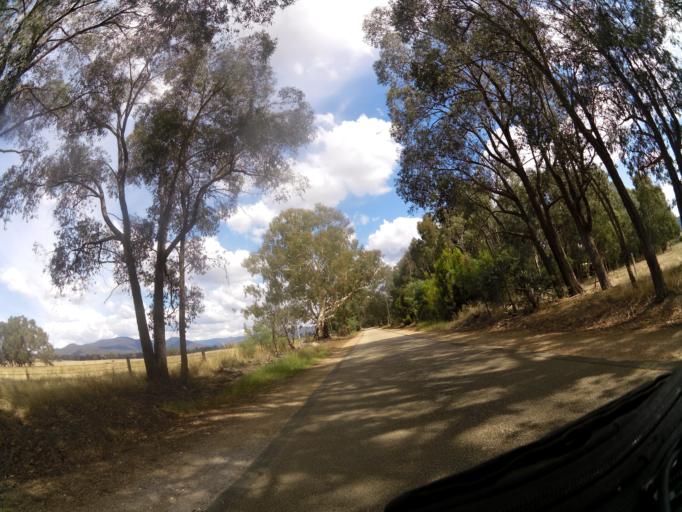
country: AU
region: Victoria
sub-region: Benalla
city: Benalla
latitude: -36.7518
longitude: 145.9817
